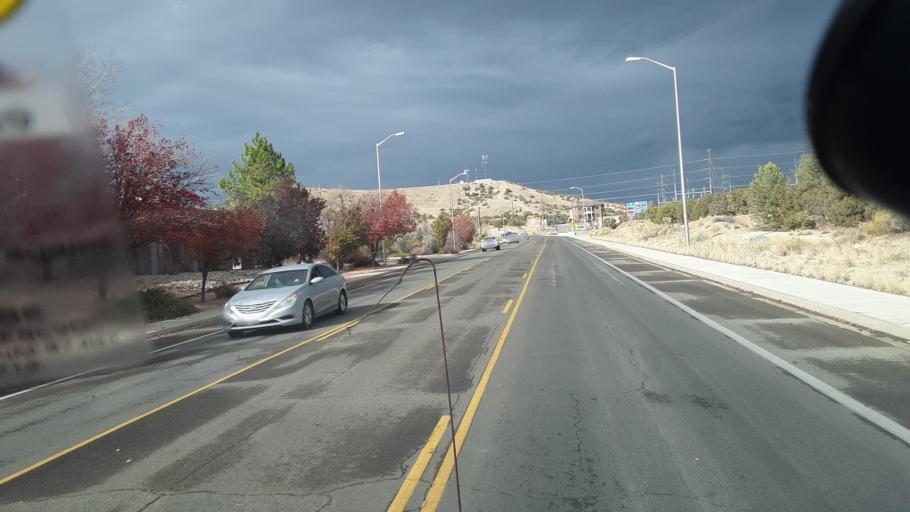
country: US
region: New Mexico
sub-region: San Juan County
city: Farmington
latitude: 36.7715
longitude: -108.1853
